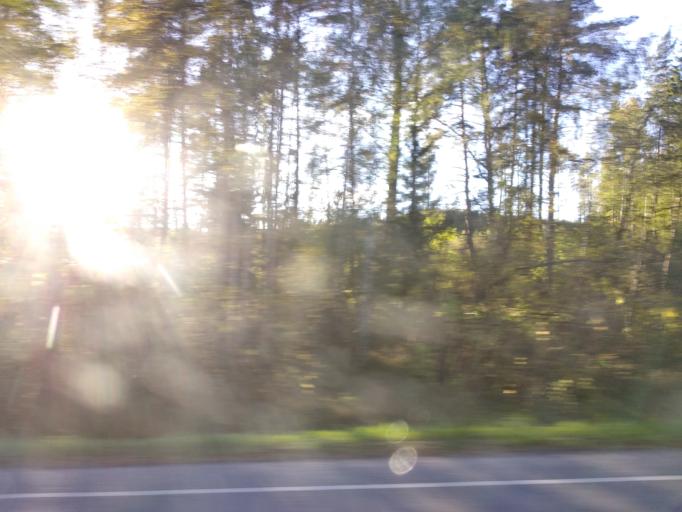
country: EE
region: Polvamaa
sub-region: Polva linn
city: Polva
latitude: 58.0452
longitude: 27.0657
